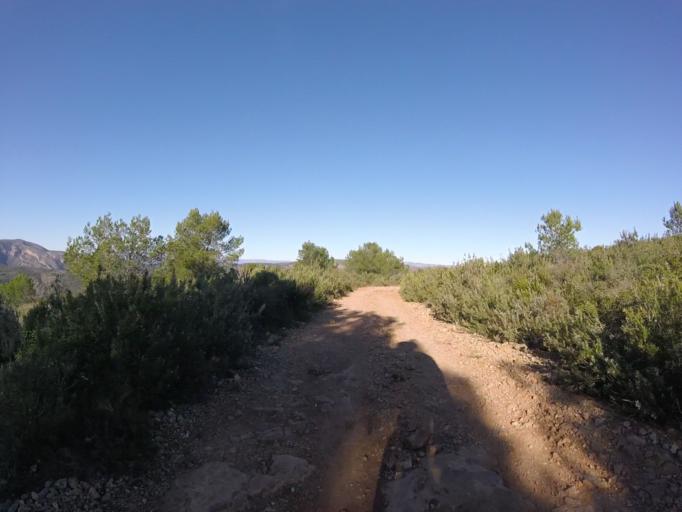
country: ES
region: Valencia
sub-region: Provincia de Castello
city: Orpesa/Oropesa del Mar
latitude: 40.0938
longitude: 0.1053
